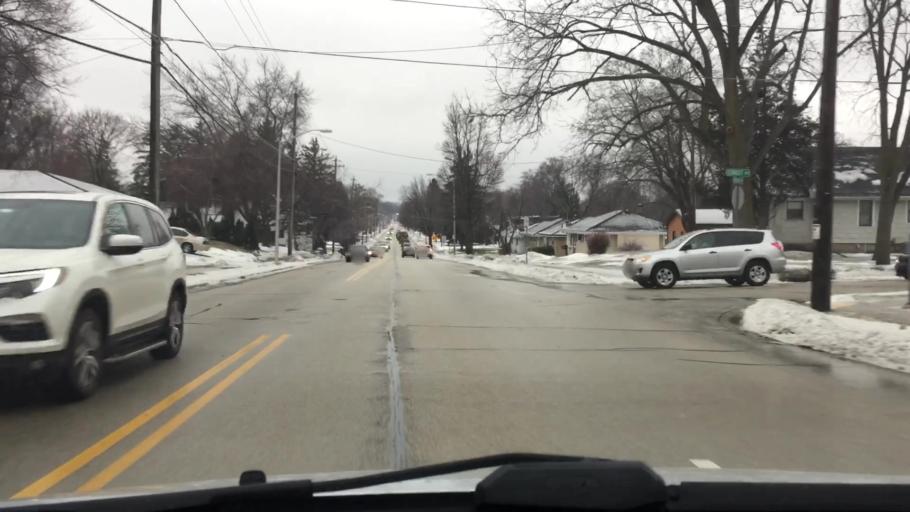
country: US
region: Wisconsin
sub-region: Waukesha County
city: Waukesha
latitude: 43.0301
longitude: -88.2560
